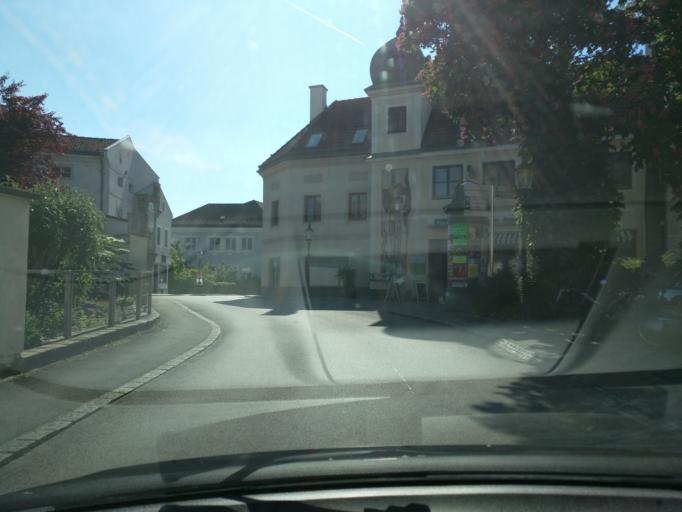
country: AT
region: Lower Austria
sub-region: Politischer Bezirk Melk
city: Ybbs an der Donau
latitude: 48.1770
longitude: 15.0836
